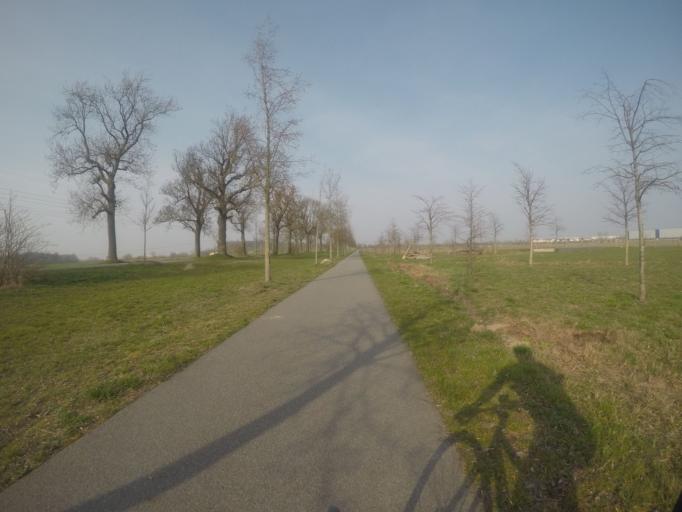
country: DE
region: Berlin
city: Rudow
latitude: 52.3895
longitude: 13.4809
